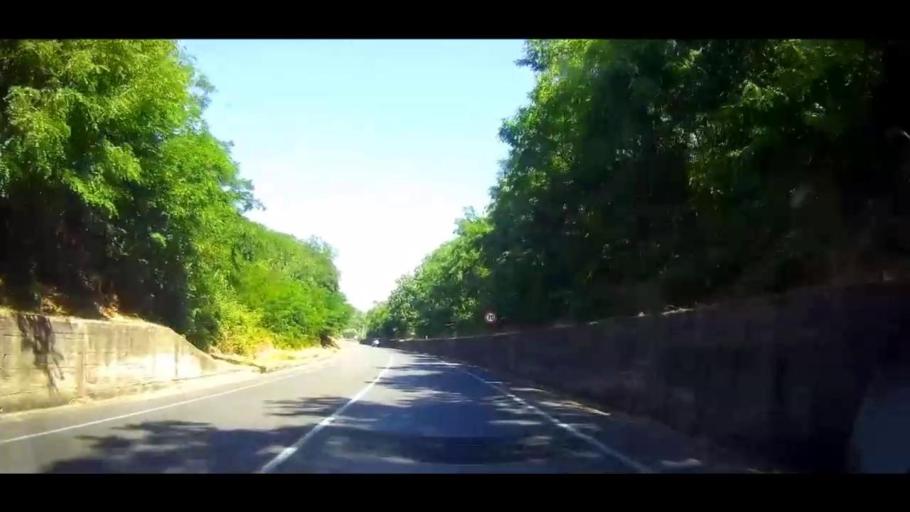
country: IT
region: Calabria
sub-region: Provincia di Cosenza
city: Zumpano
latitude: 39.2994
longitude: 16.2852
